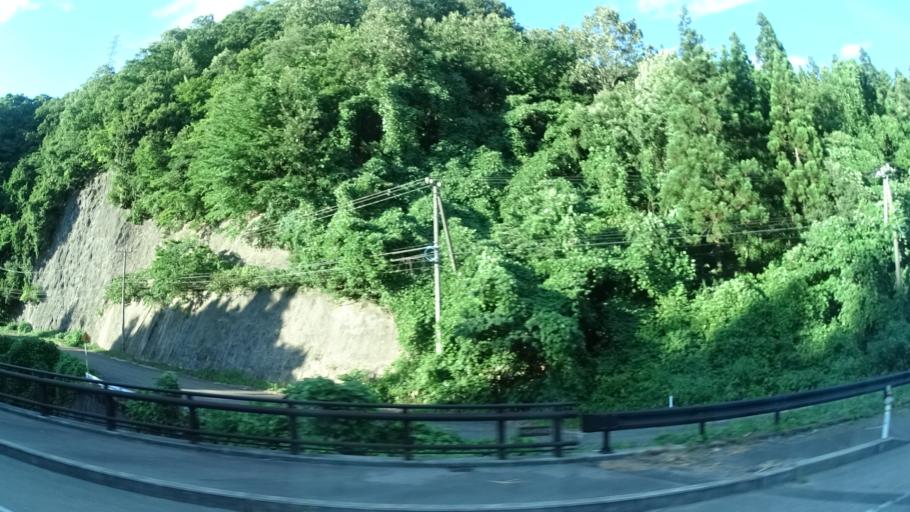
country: JP
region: Ishikawa
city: Nanao
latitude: 37.2497
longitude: 136.8896
